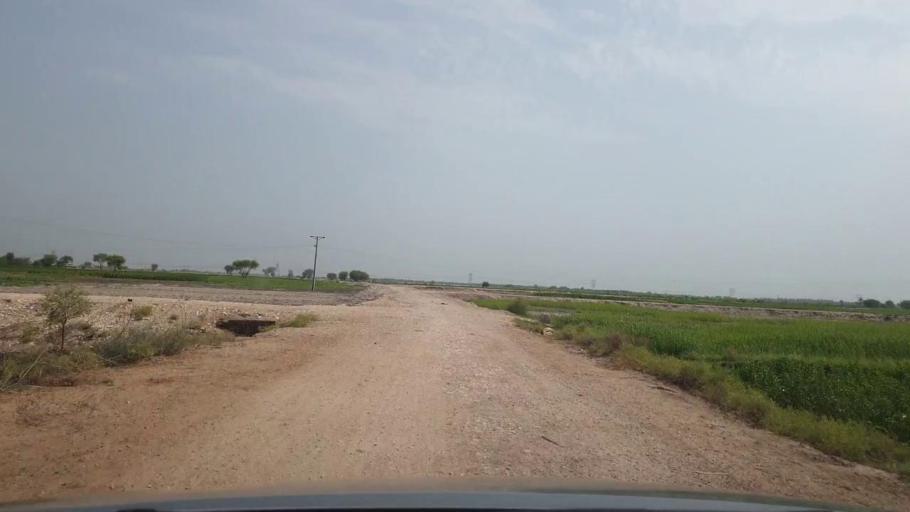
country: PK
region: Sindh
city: Rohri
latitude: 27.6609
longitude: 69.0256
